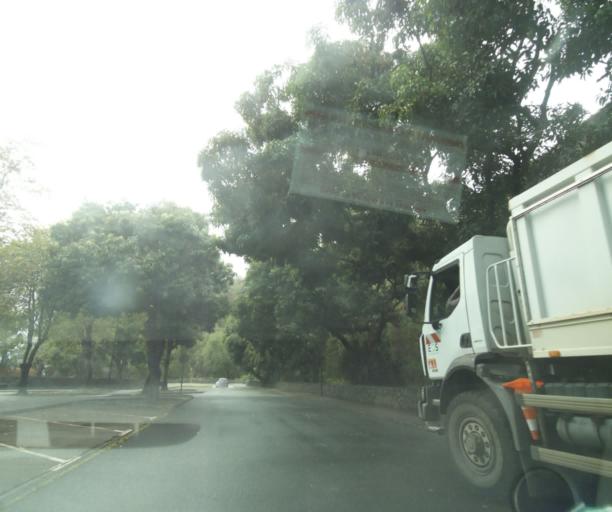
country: RE
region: Reunion
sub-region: Reunion
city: Saint-Paul
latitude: -21.0163
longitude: 55.2601
